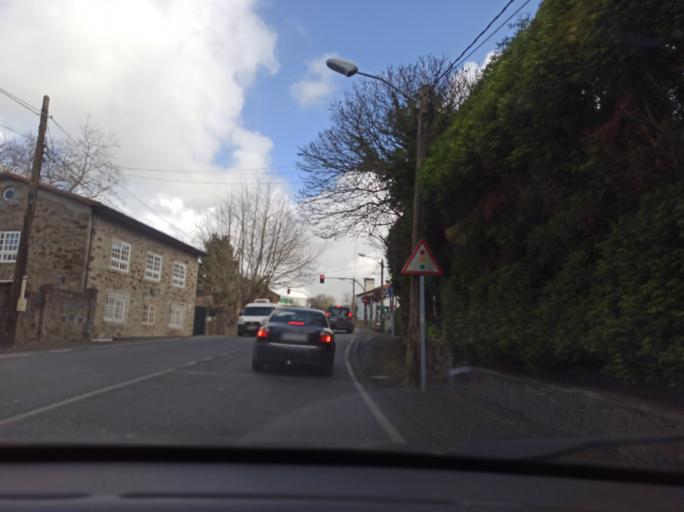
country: ES
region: Galicia
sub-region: Provincia da Coruna
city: Oleiros
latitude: 43.3330
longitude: -8.3083
